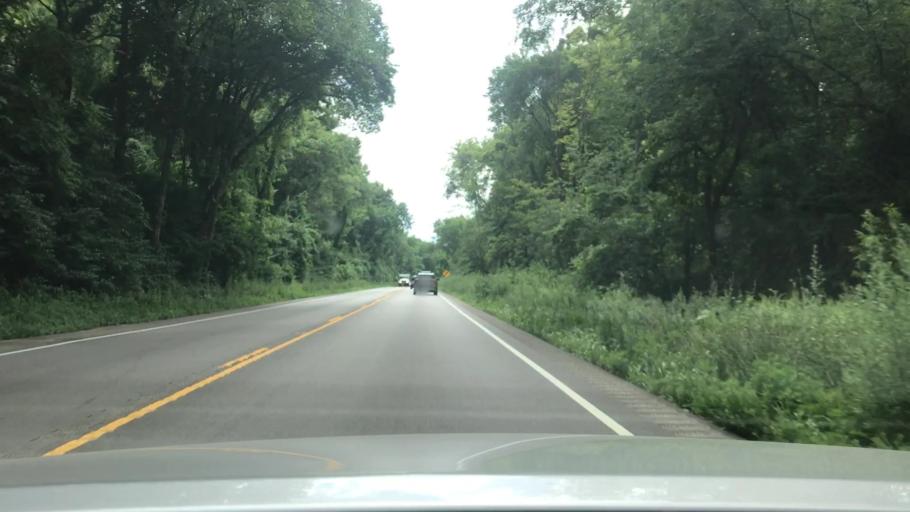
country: US
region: Illinois
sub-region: DuPage County
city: Burr Ridge
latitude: 41.7055
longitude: -87.9230
